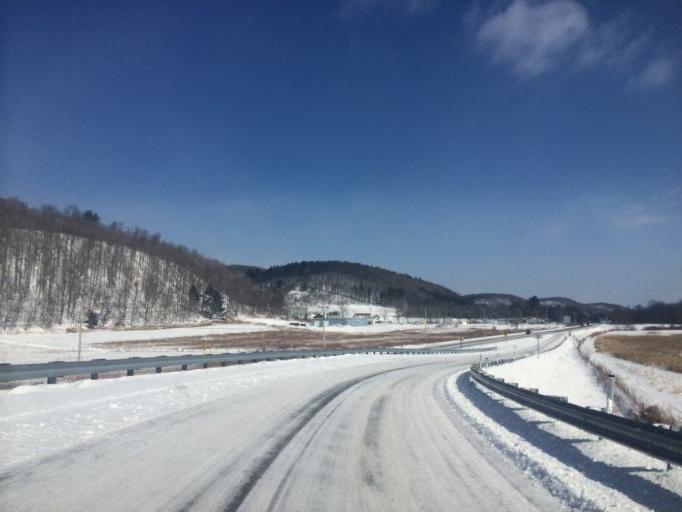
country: US
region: Pennsylvania
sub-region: Centre County
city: Stormstown
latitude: 40.8297
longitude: -78.0148
